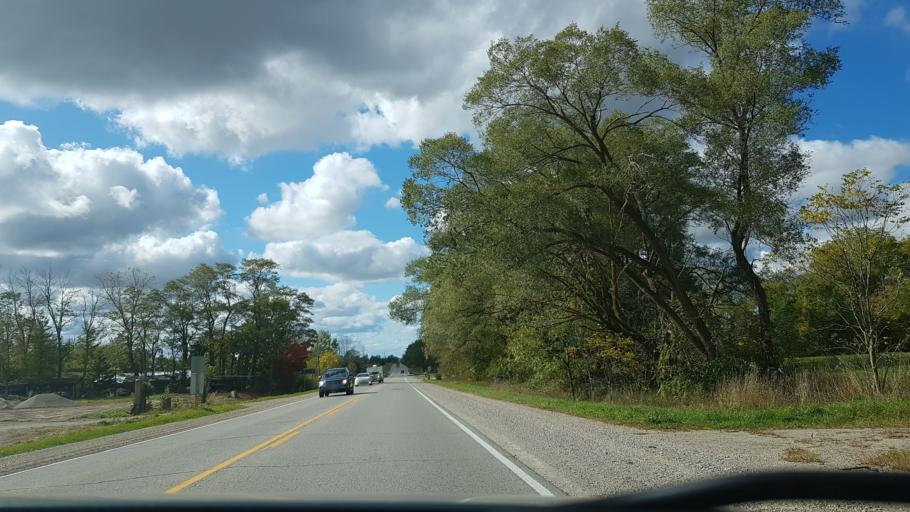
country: CA
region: Ontario
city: South Huron
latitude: 43.3606
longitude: -81.4946
